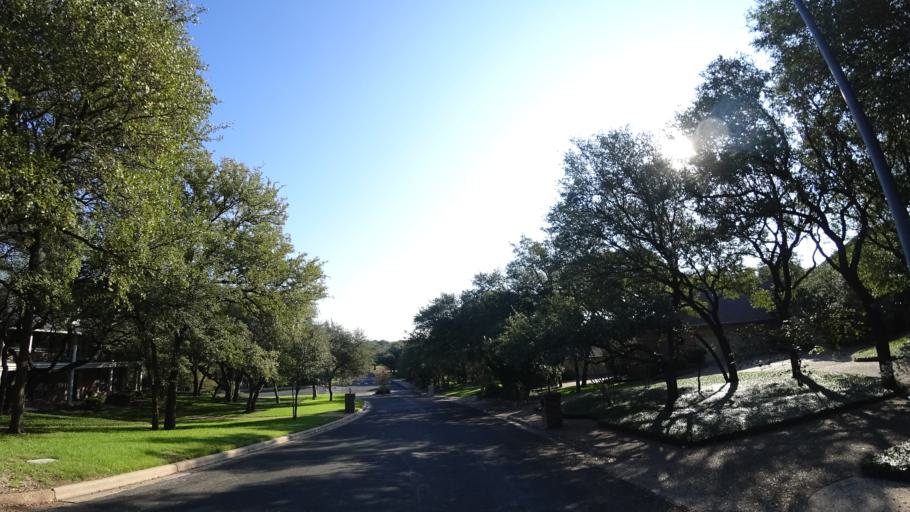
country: US
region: Texas
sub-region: Travis County
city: Rollingwood
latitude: 30.2648
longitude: -97.7943
